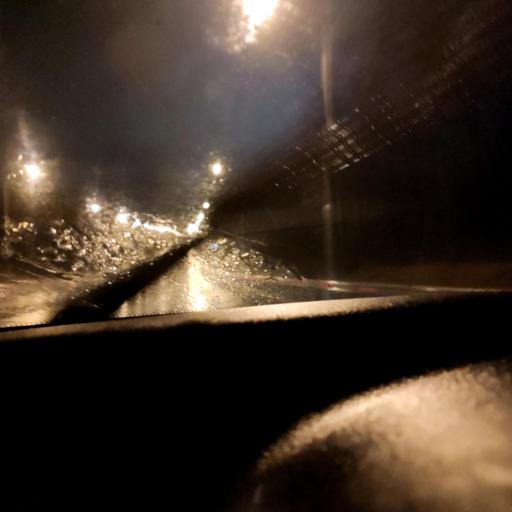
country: RU
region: Samara
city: Petra-Dubrava
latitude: 53.2899
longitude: 50.2483
